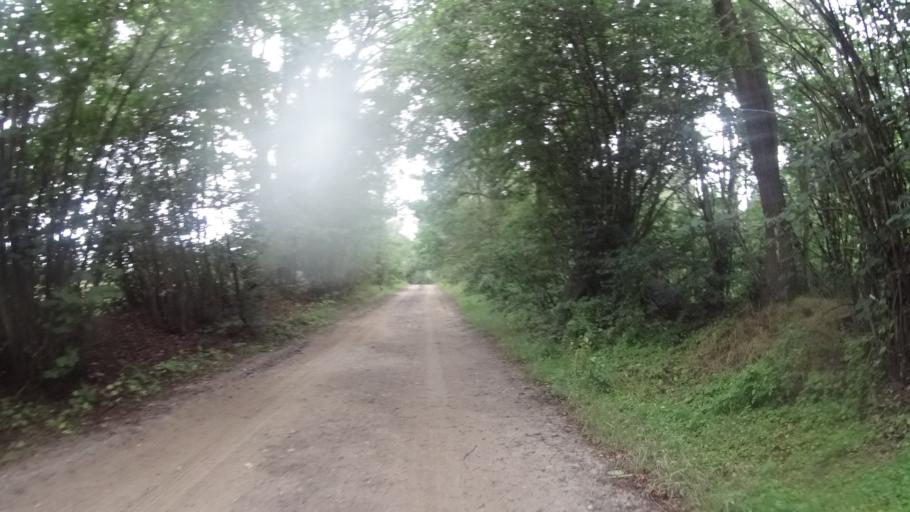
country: DE
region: Schleswig-Holstein
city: Dalldorf
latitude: 53.4127
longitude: 10.6094
